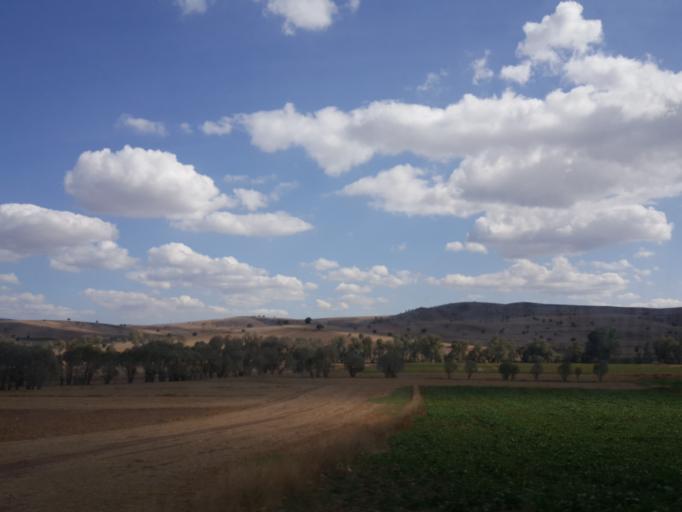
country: TR
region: Tokat
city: Camlibel
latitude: 40.1731
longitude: 36.4389
